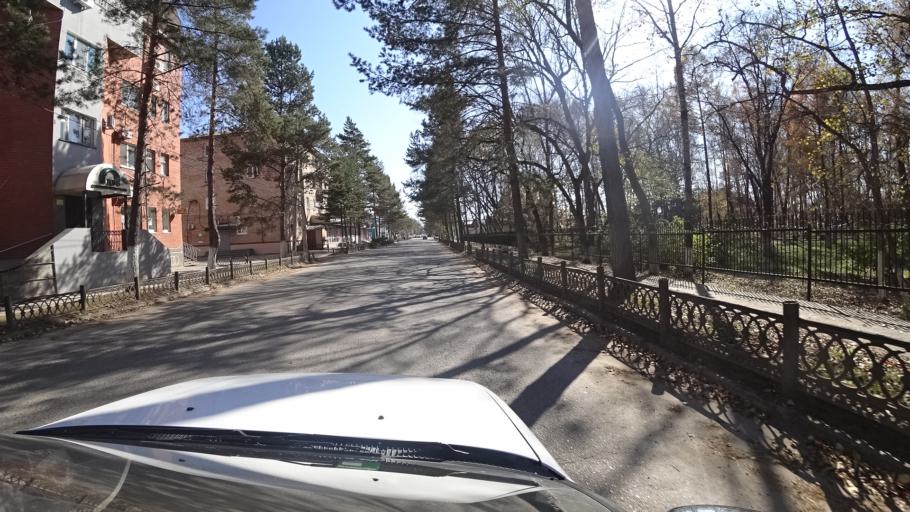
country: RU
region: Primorskiy
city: Dal'nerechensk
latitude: 45.9315
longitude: 133.7306
